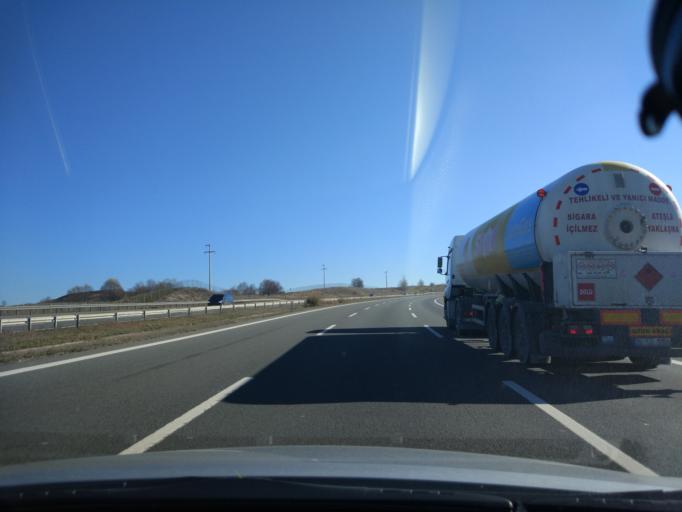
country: TR
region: Bolu
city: Yenicaga
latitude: 40.7640
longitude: 32.0564
